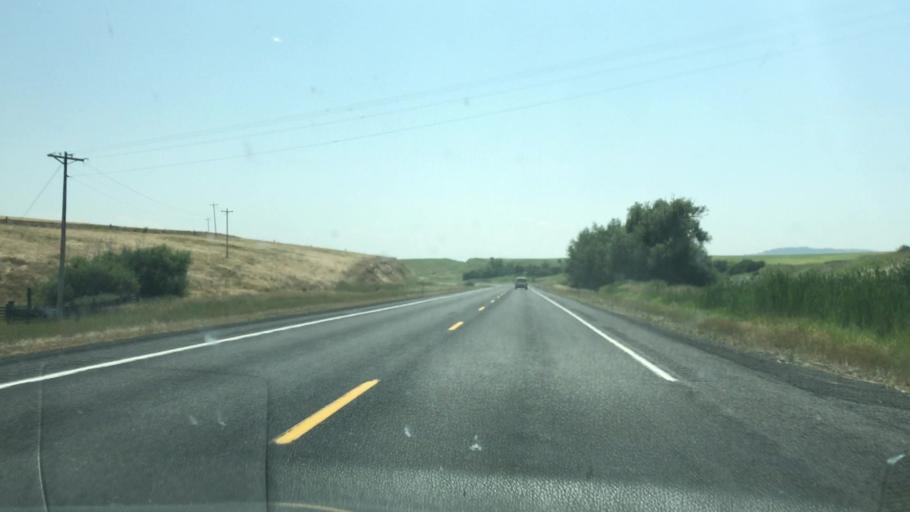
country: US
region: Idaho
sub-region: Lewis County
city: Nezperce
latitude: 46.2238
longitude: -116.4384
